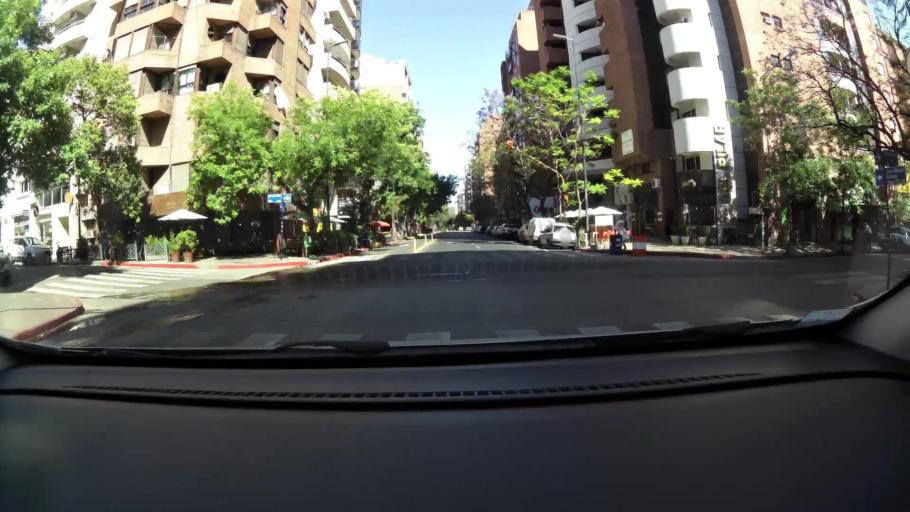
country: AR
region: Cordoba
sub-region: Departamento de Capital
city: Cordoba
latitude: -31.4278
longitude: -64.1874
